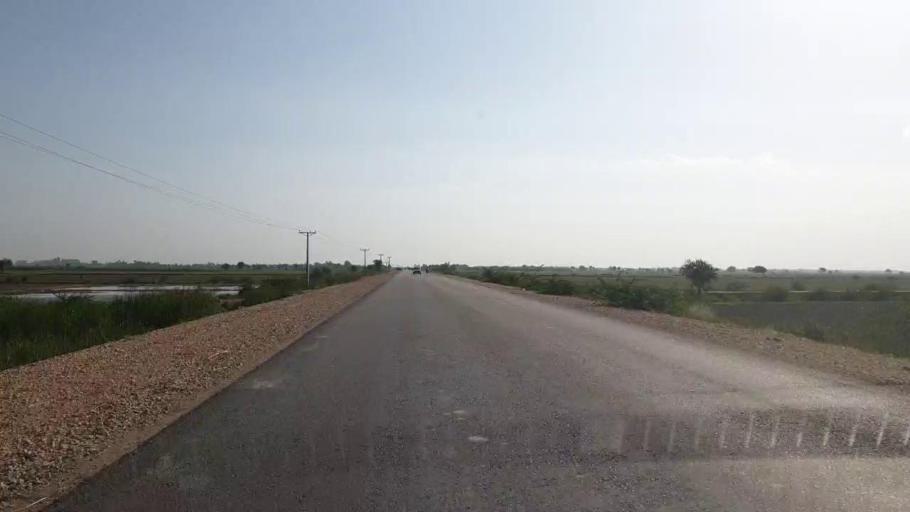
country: PK
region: Sindh
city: Tando Bago
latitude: 24.6574
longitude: 68.9977
